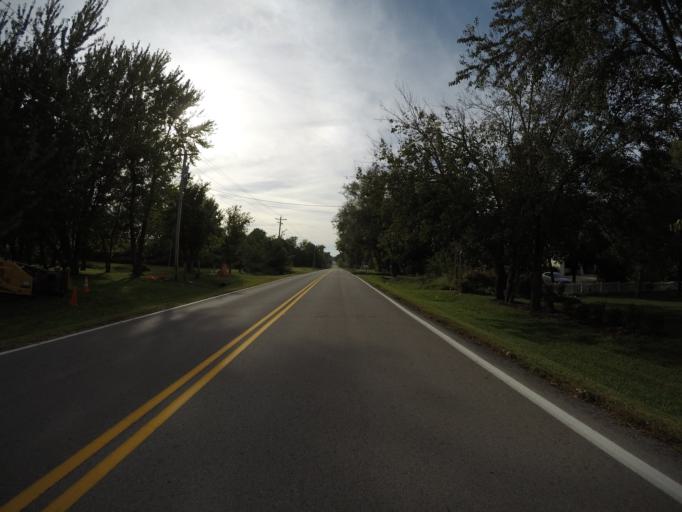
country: US
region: Kansas
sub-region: Douglas County
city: Baldwin City
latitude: 38.7750
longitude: -95.1750
